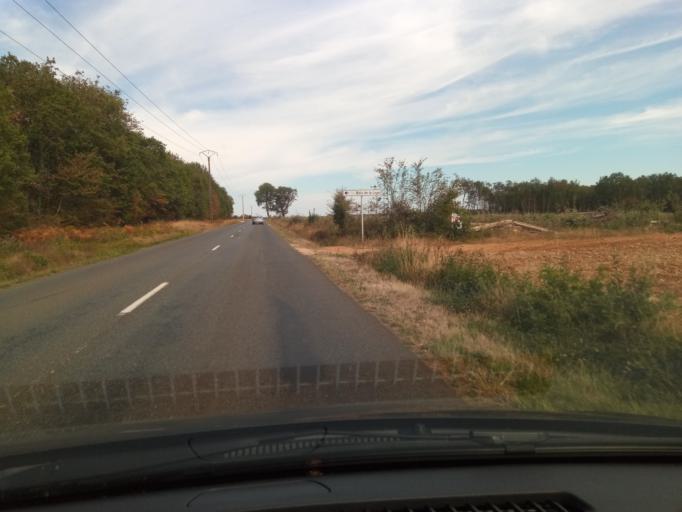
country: FR
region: Poitou-Charentes
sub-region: Departement de la Vienne
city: Chauvigny
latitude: 46.5511
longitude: 0.6043
